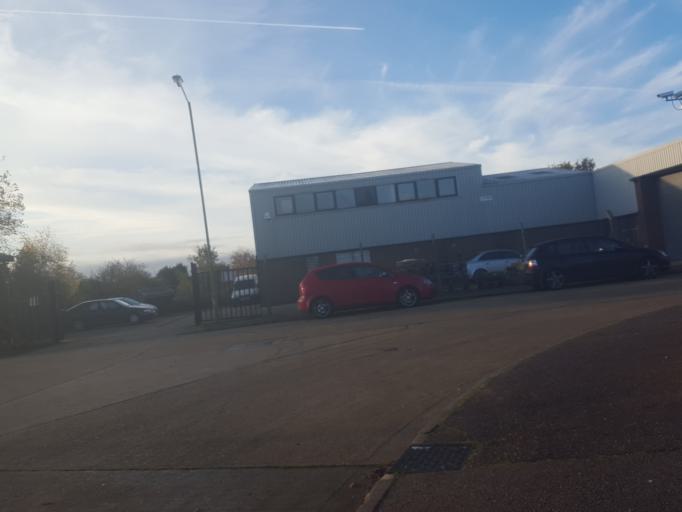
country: GB
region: England
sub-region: Essex
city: Little Clacton
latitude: 51.8167
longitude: 1.1701
